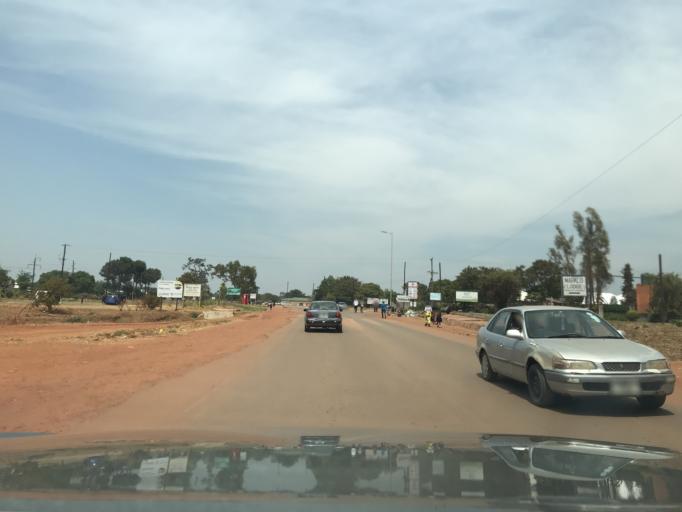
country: ZM
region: Northern
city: Kasama
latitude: -10.2050
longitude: 31.1818
